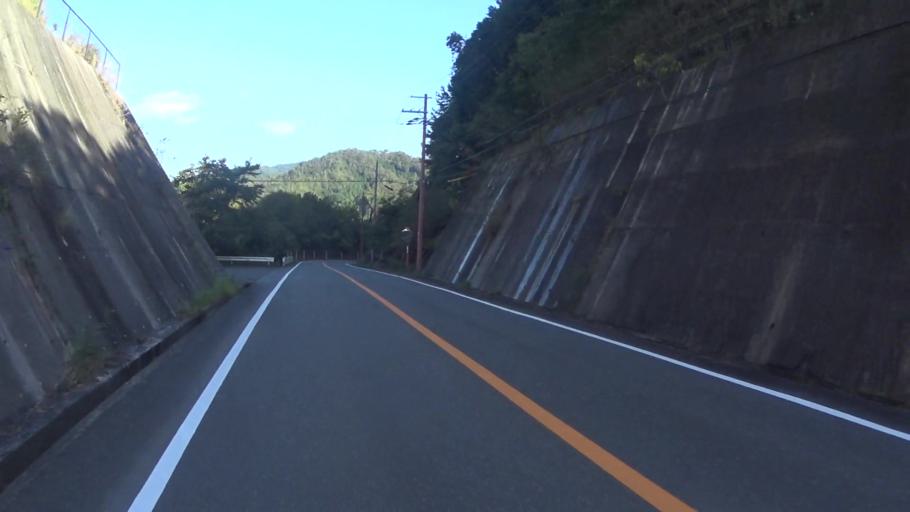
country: JP
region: Kyoto
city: Kameoka
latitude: 35.1320
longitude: 135.5389
